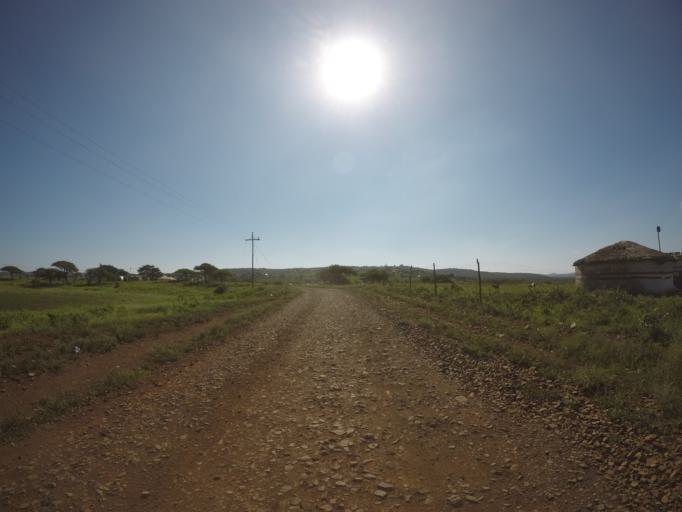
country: ZA
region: KwaZulu-Natal
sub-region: uThungulu District Municipality
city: Empangeni
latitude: -28.5721
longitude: 31.7257
